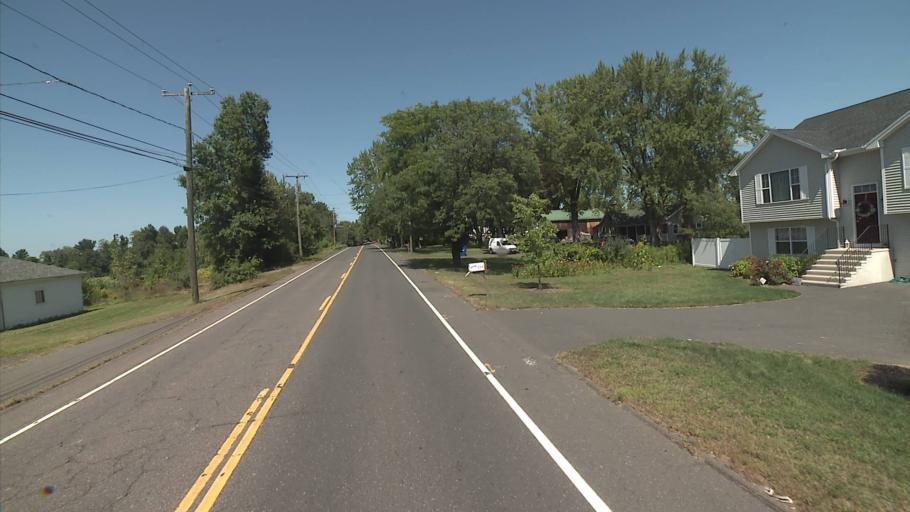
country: US
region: Connecticut
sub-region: Hartford County
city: Windsor Locks
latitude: 41.9529
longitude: -72.6276
